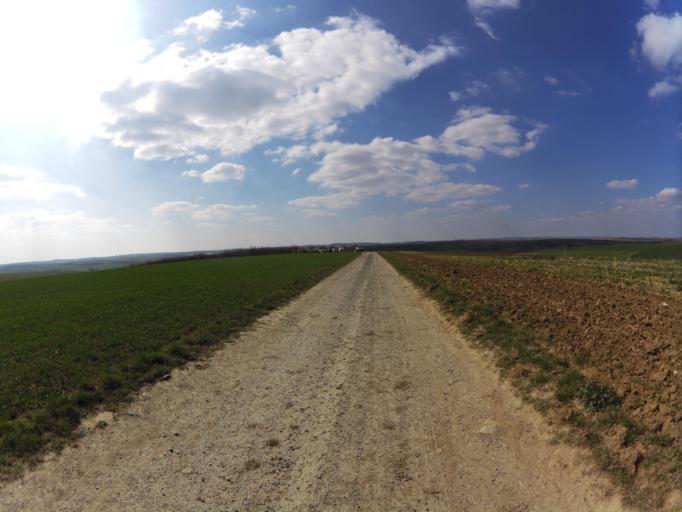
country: DE
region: Bavaria
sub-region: Regierungsbezirk Unterfranken
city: Dettelbach
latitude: 49.8307
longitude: 10.1620
